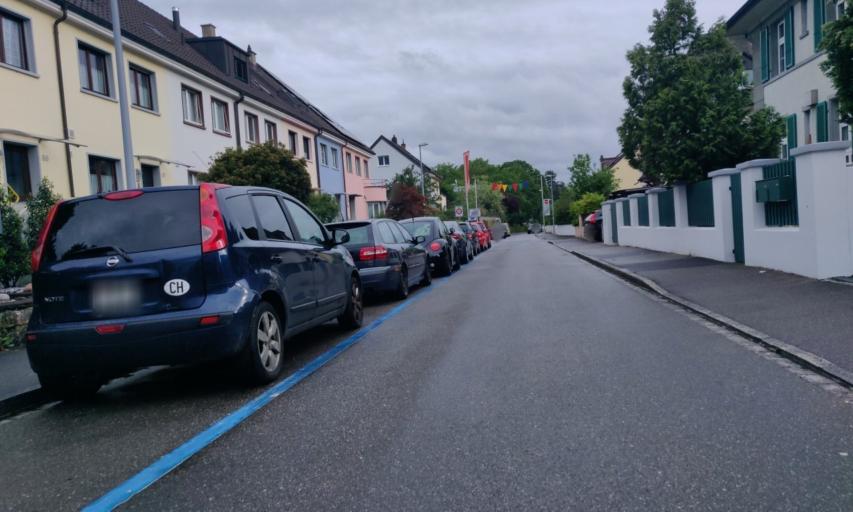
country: CH
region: Basel-City
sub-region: Basel-Stadt
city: Riehen
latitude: 47.5738
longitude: 7.6349
